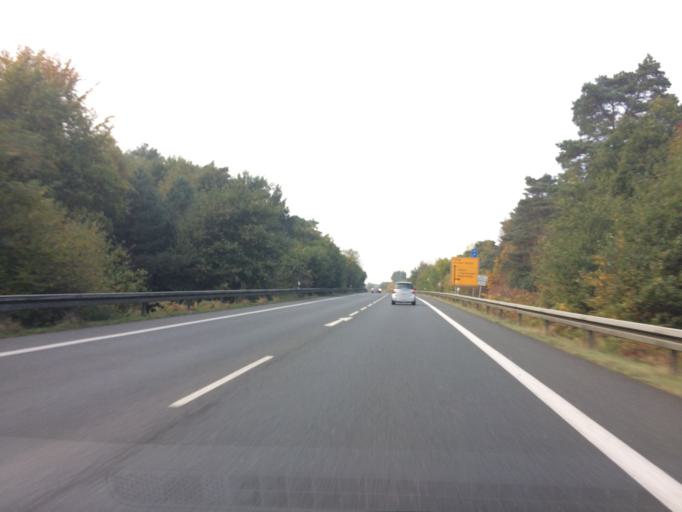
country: DE
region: North Rhine-Westphalia
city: Dorsten
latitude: 51.6823
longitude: 7.0231
